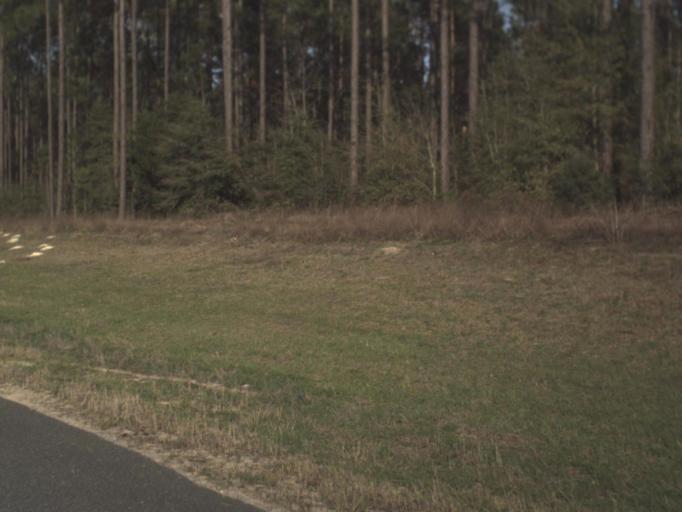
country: US
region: Florida
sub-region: Calhoun County
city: Blountstown
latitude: 30.5177
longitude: -85.1971
